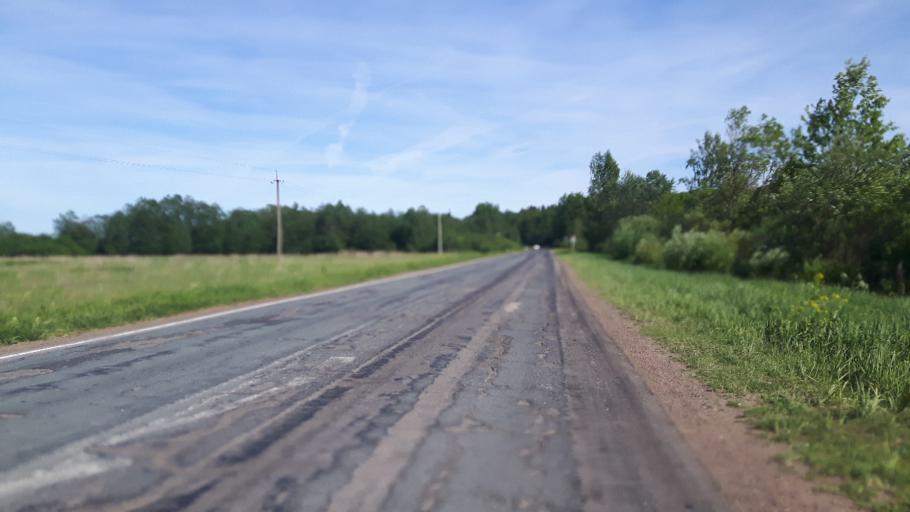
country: RU
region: Leningrad
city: Ivangorod
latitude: 59.4179
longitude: 28.3630
